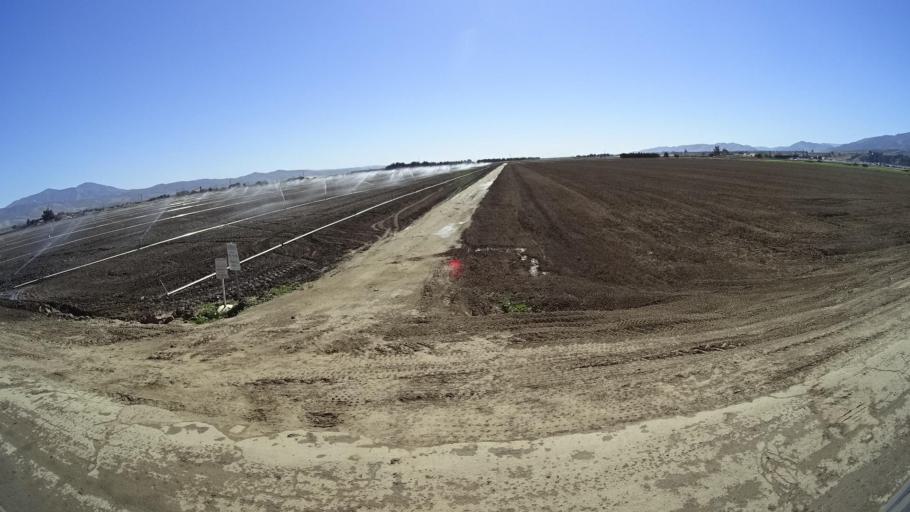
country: US
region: California
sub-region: Monterey County
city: Soledad
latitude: 36.3967
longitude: -121.3441
